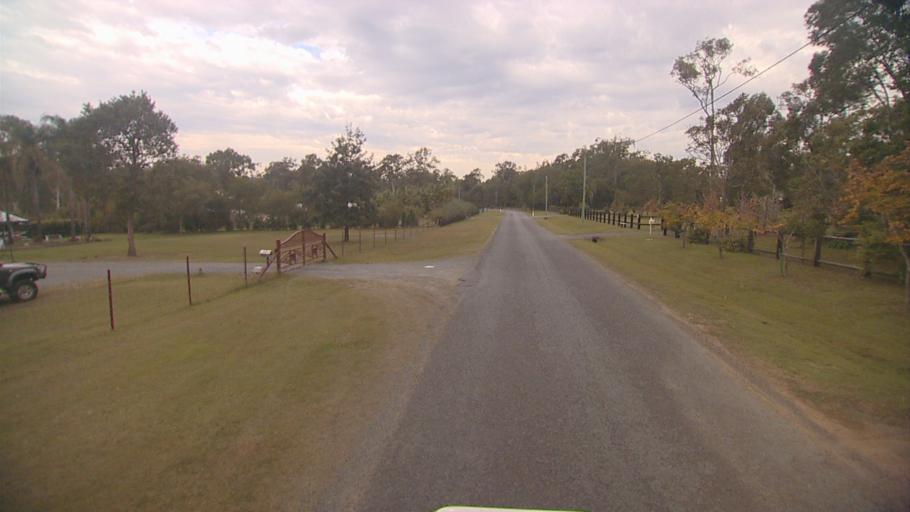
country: AU
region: Queensland
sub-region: Logan
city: Chambers Flat
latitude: -27.7919
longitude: 153.1114
